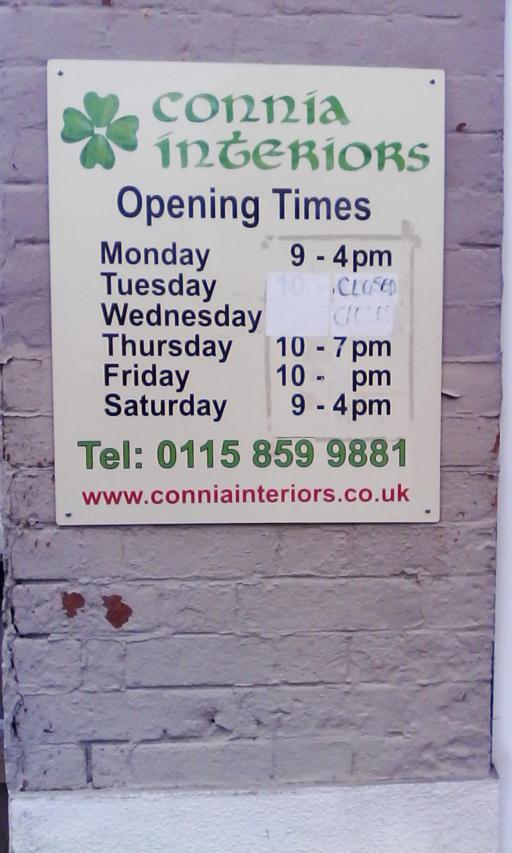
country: GB
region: England
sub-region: Nottinghamshire
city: Arnold
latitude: 52.9701
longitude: -1.1198
